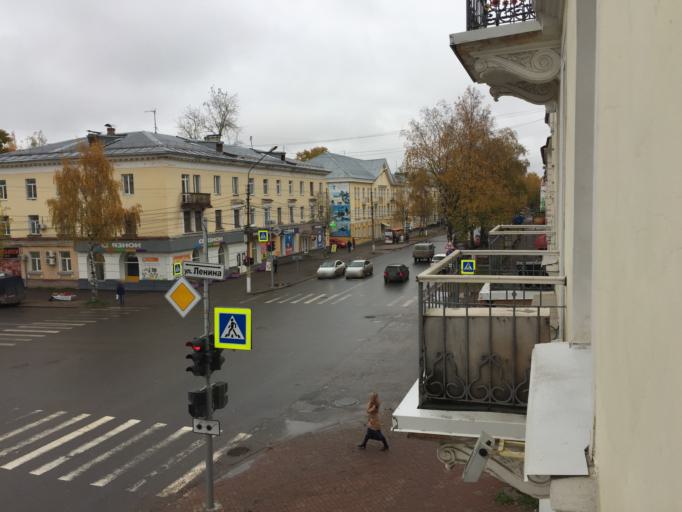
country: RU
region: Komi Republic
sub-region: Syktyvdinskiy Rayon
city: Syktyvkar
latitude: 61.6727
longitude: 50.8322
